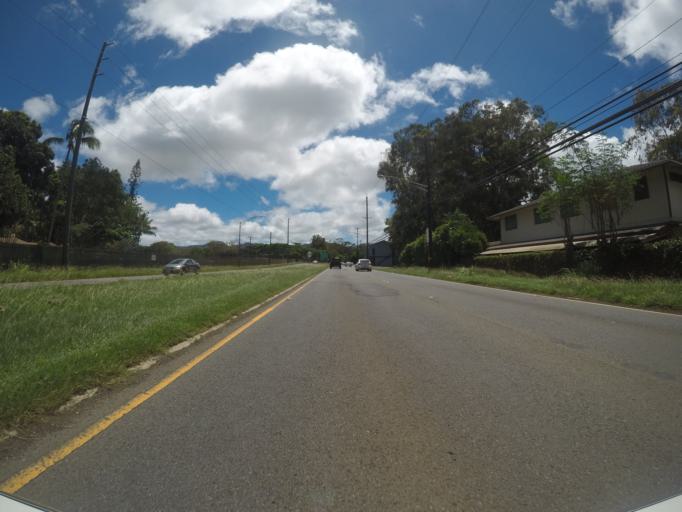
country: US
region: Hawaii
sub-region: Honolulu County
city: Wahiawa
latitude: 21.4892
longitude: -158.0361
